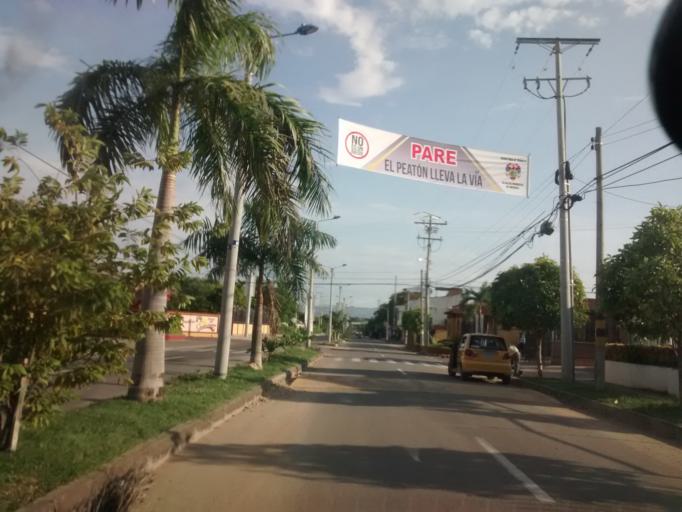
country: CO
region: Cundinamarca
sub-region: Girardot
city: Girardot City
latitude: 4.3088
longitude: -74.8149
